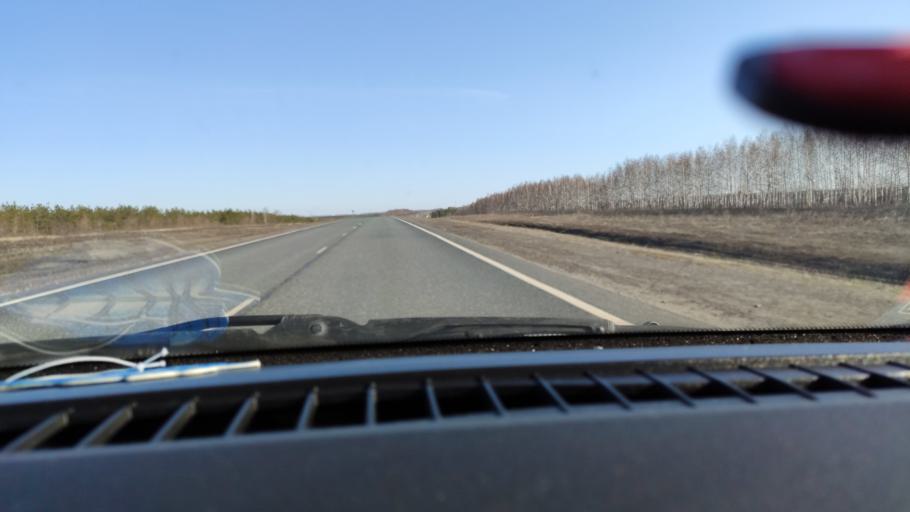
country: RU
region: Samara
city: Syzran'
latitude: 52.8936
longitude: 48.2949
